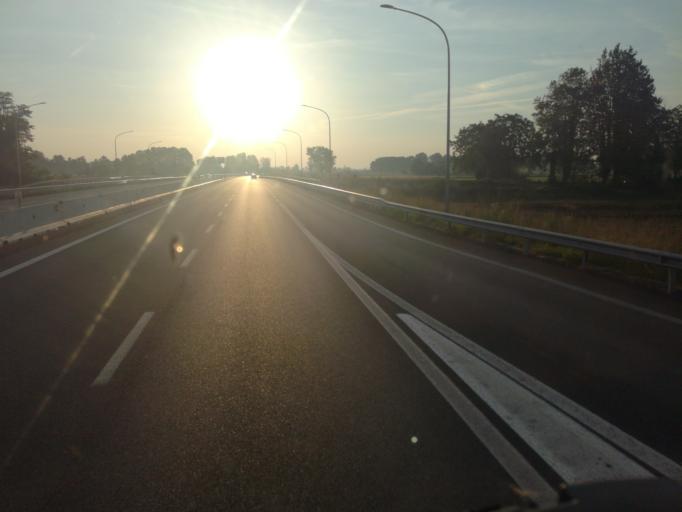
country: IT
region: Lombardy
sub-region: Provincia di Cremona
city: Spino d'Adda
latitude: 45.3915
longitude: 9.4959
